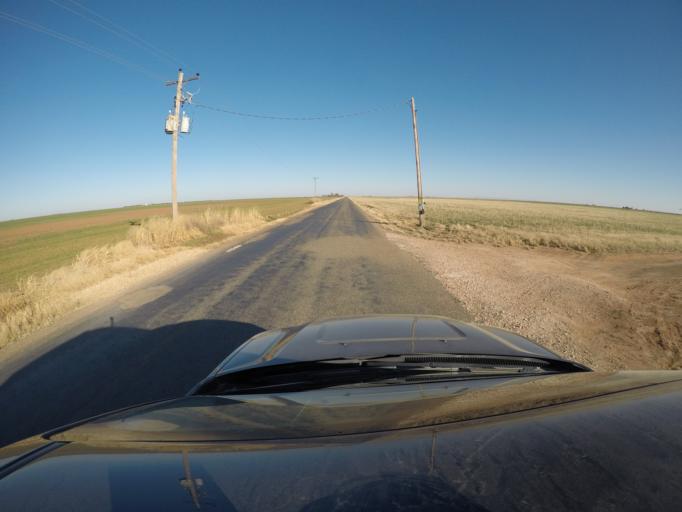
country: US
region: Texas
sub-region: Parmer County
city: Farwell
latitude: 34.3026
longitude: -103.0694
